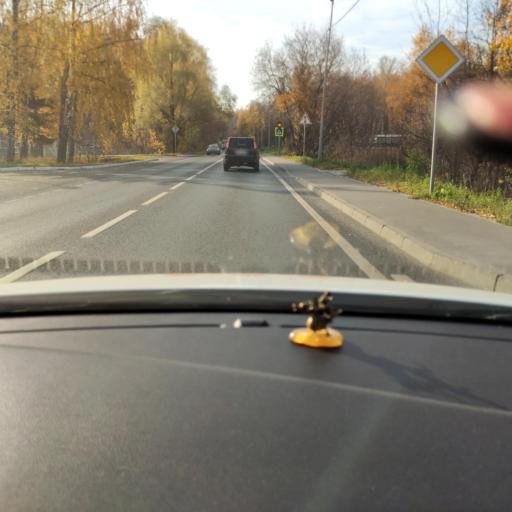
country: RU
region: Tatarstan
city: Osinovo
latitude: 55.8446
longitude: 48.8924
